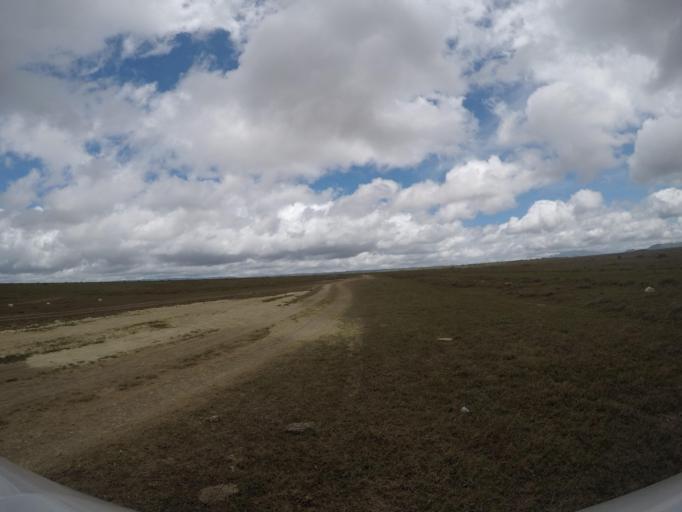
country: TL
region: Lautem
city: Lospalos
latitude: -8.4497
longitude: 126.9866
